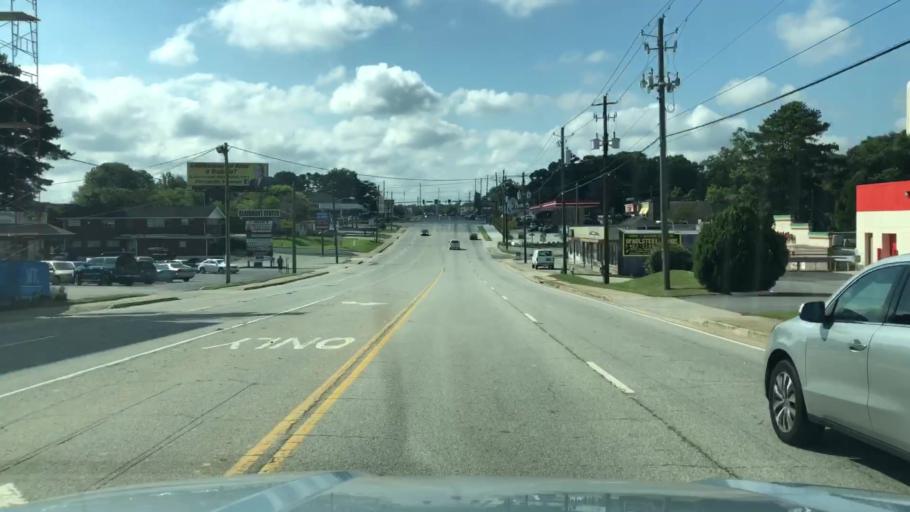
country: US
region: Georgia
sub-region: DeKalb County
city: Chamblee
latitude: 33.8677
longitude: -84.3095
